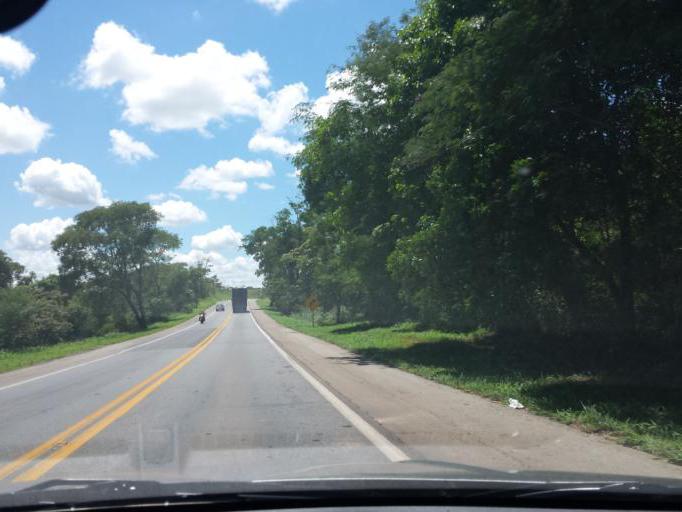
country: BR
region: Goias
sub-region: Cristalina
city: Cristalina
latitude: -16.5320
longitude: -47.8024
